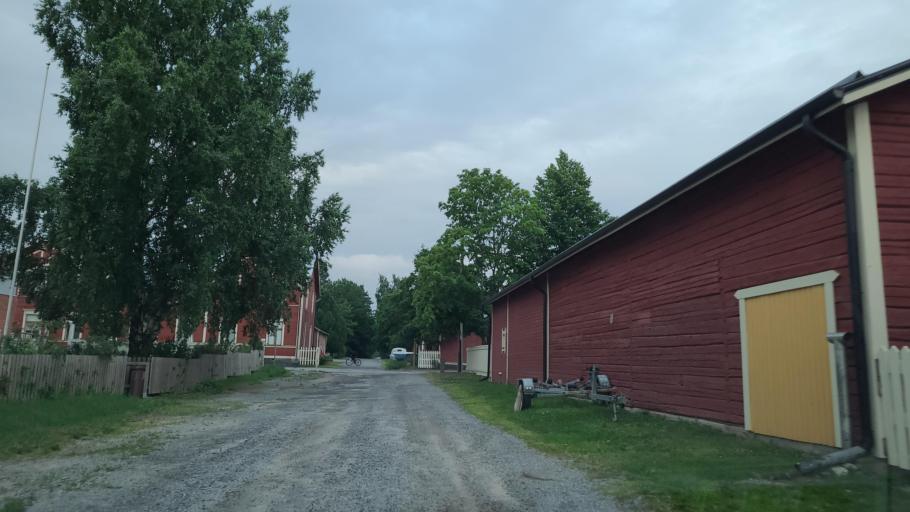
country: FI
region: Ostrobothnia
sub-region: Vaasa
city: Vaasa
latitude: 63.1035
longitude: 21.6141
